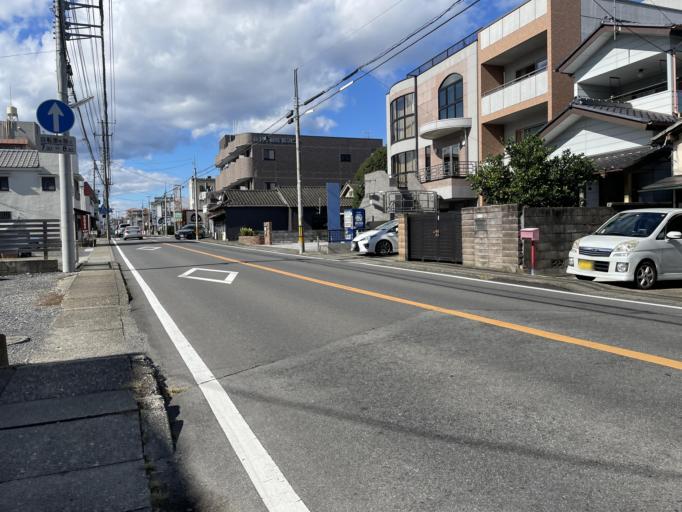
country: JP
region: Ibaraki
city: Mito-shi
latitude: 36.3847
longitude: 140.4604
